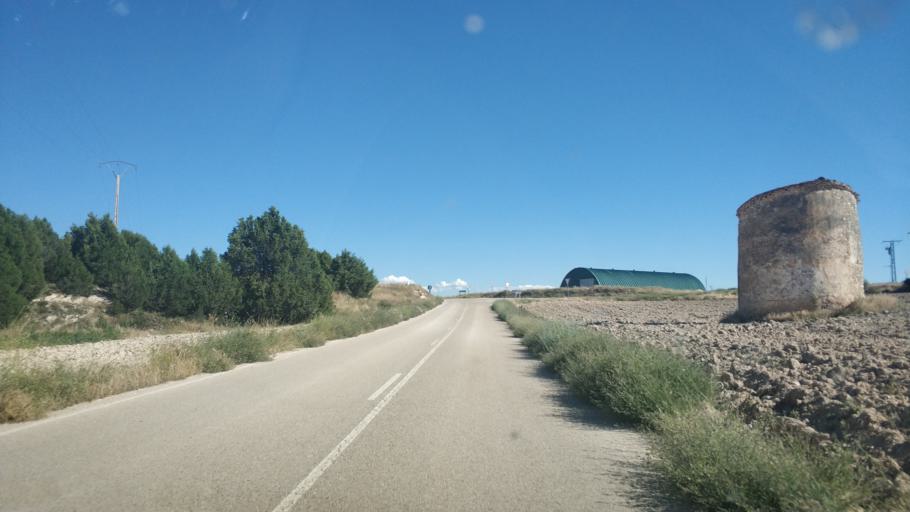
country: ES
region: Castille and Leon
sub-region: Provincia de Soria
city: Liceras
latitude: 41.4630
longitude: -3.2143
